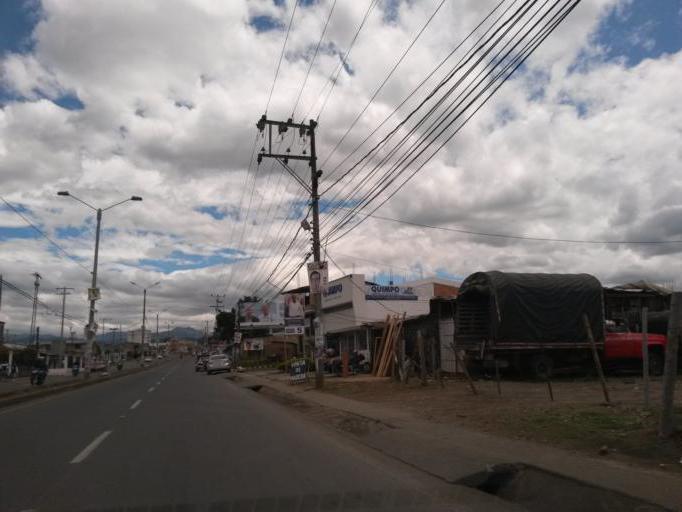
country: CO
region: Cauca
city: Popayan
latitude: 2.4812
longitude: -76.5726
